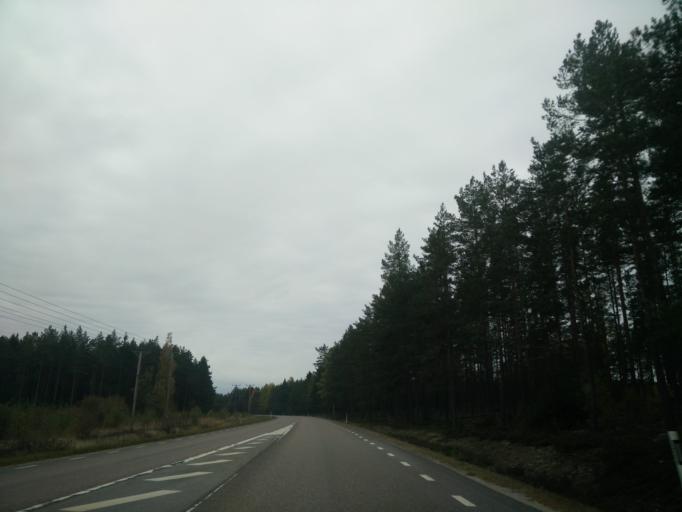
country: SE
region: Gaevleborg
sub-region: Gavle Kommun
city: Gavle
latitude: 60.7881
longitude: 17.2021
